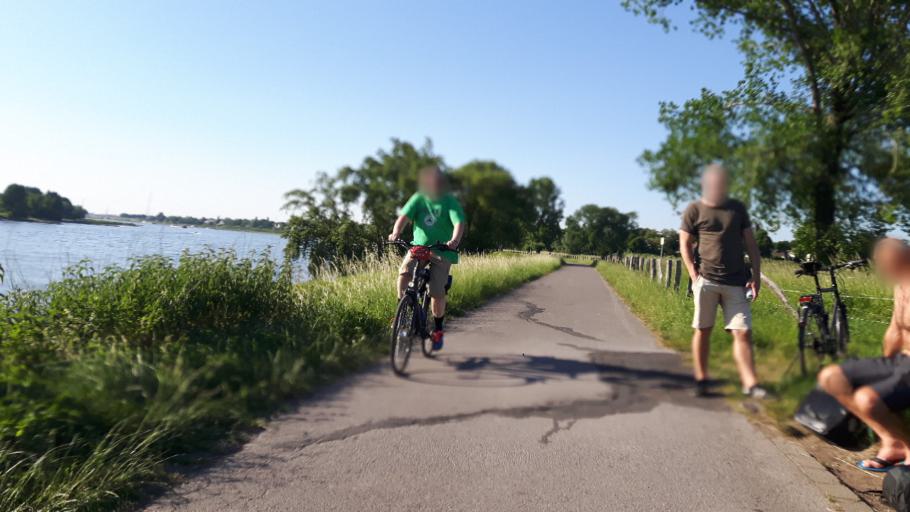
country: DE
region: North Rhine-Westphalia
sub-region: Regierungsbezirk Dusseldorf
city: Meerbusch
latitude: 51.3164
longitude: 6.7372
